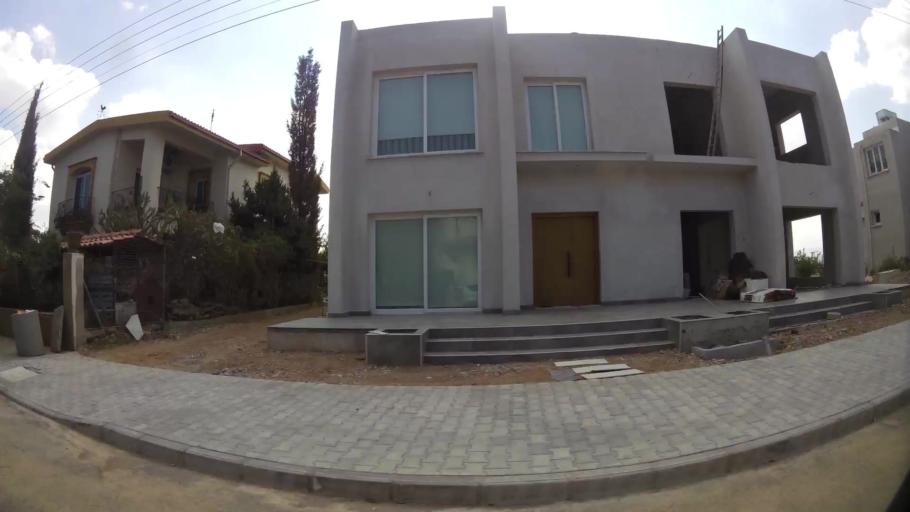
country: CY
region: Lefkosia
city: Nicosia
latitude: 35.2250
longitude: 33.2907
